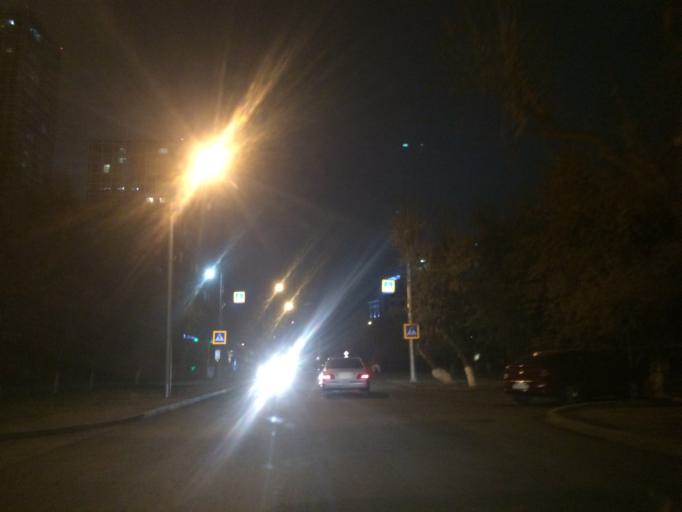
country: KZ
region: Astana Qalasy
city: Astana
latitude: 51.1637
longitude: 71.4173
